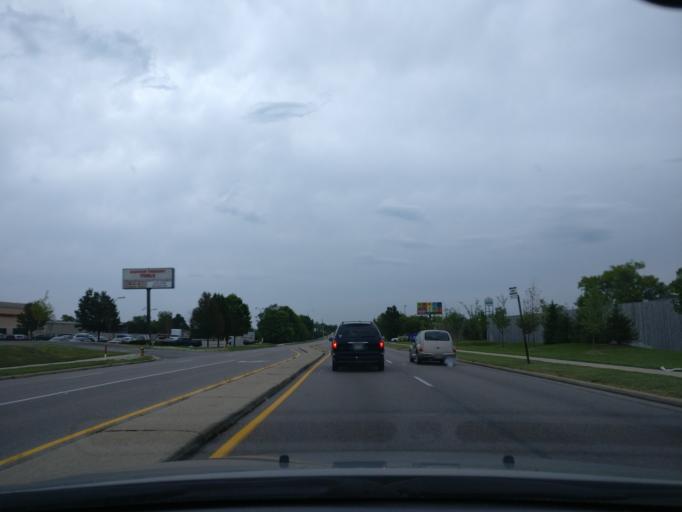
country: US
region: Ohio
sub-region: Montgomery County
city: West Carrollton City
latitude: 39.6281
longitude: -84.2243
